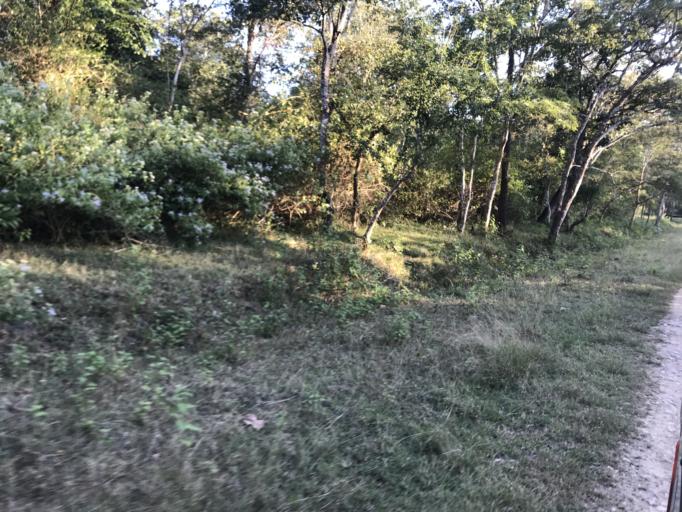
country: IN
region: Karnataka
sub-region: Mysore
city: Heggadadevankote
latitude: 11.9974
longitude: 76.2454
